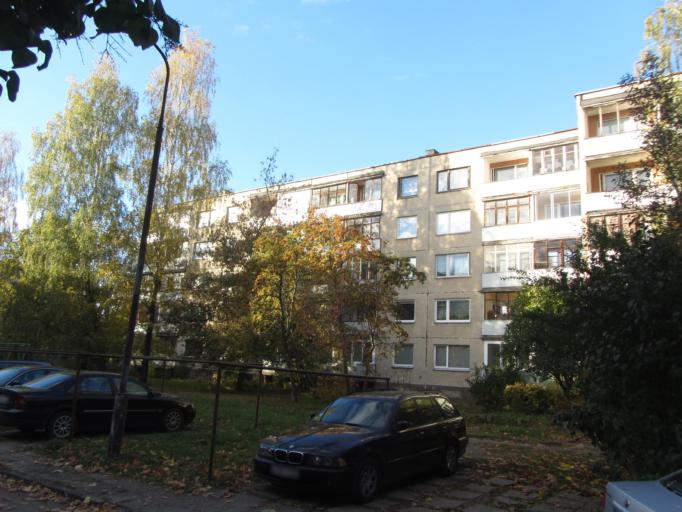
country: LT
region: Vilnius County
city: Lazdynai
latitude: 54.6734
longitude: 25.2119
